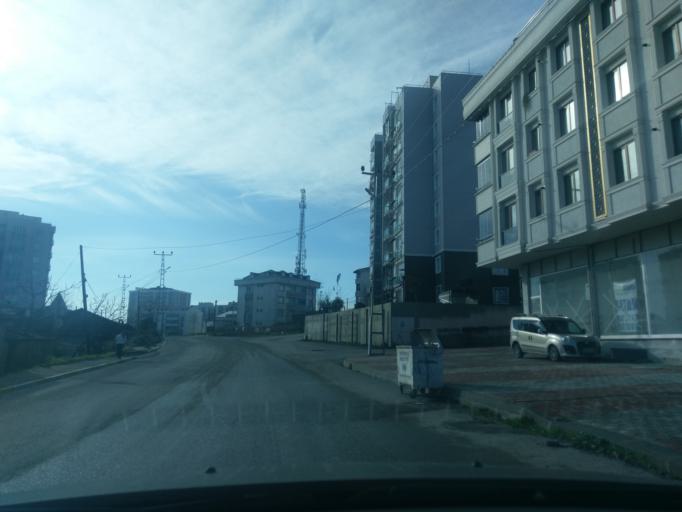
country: TR
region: Istanbul
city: Sultangazi
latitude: 41.1325
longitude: 28.8385
